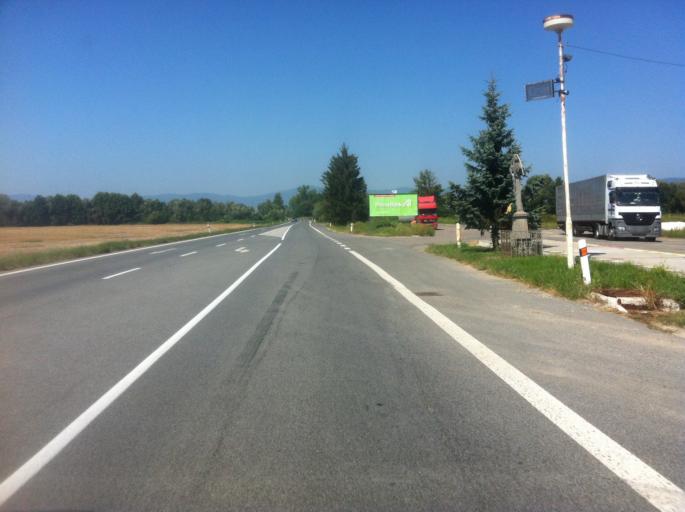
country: SK
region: Kosicky
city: Sobrance
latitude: 48.7191
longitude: 22.2169
